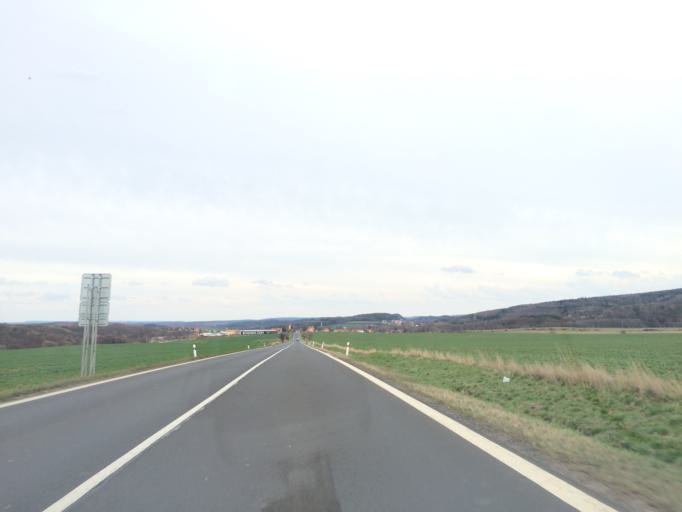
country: CZ
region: Ustecky
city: Lubenec
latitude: 50.1325
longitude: 13.2901
